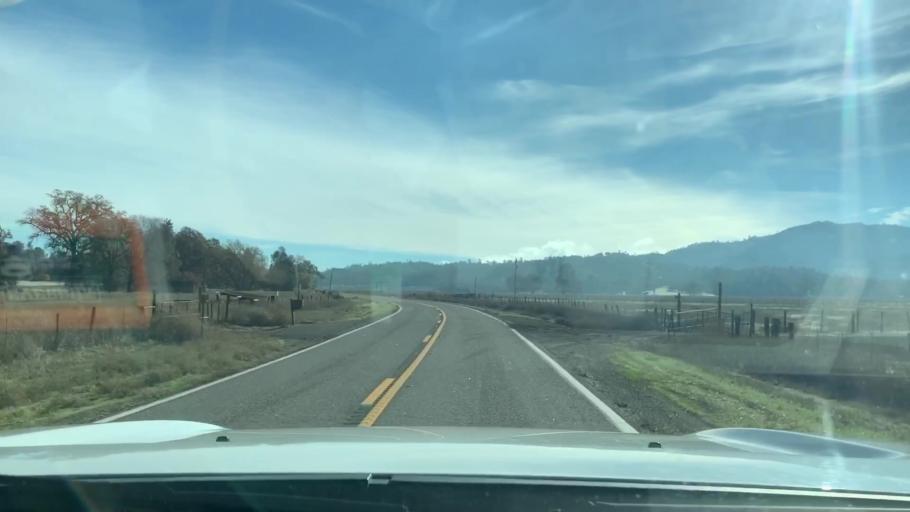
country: US
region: California
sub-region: Fresno County
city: Coalinga
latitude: 36.1782
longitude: -120.6917
